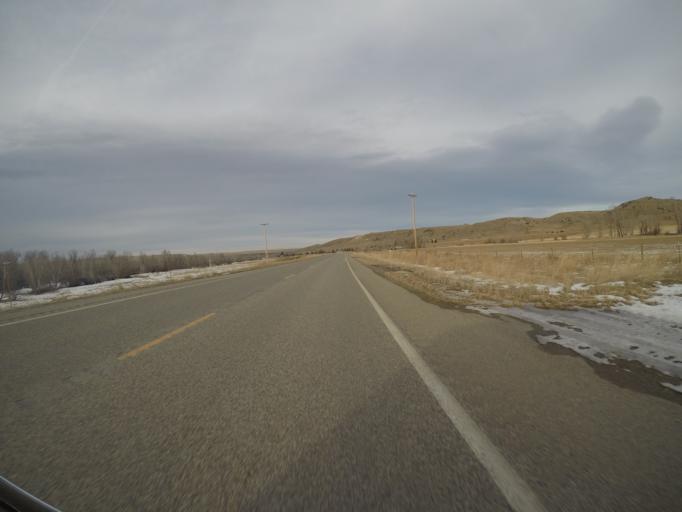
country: US
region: Montana
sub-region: Stillwater County
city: Absarokee
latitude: 45.4717
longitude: -109.4486
